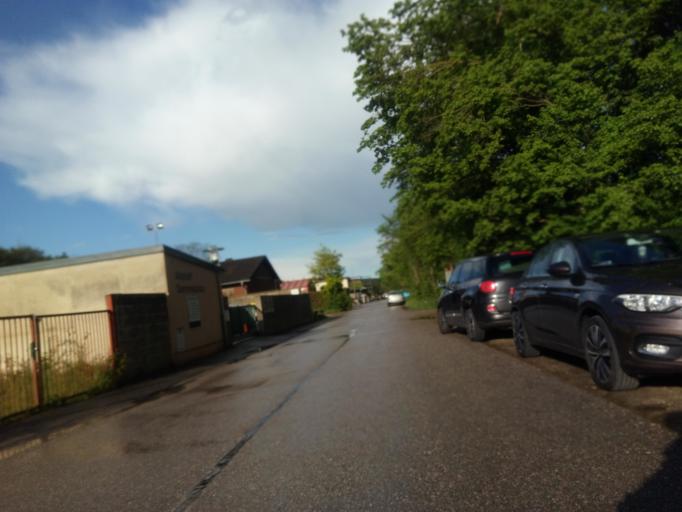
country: AT
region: Lower Austria
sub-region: Politischer Bezirk Modling
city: Laab im Walde
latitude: 48.1350
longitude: 16.1834
